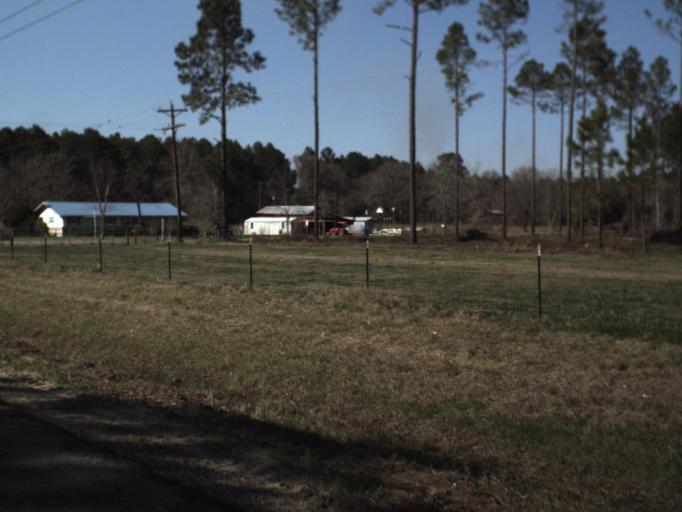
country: US
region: Florida
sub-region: Calhoun County
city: Blountstown
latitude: 30.4684
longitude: -85.0819
